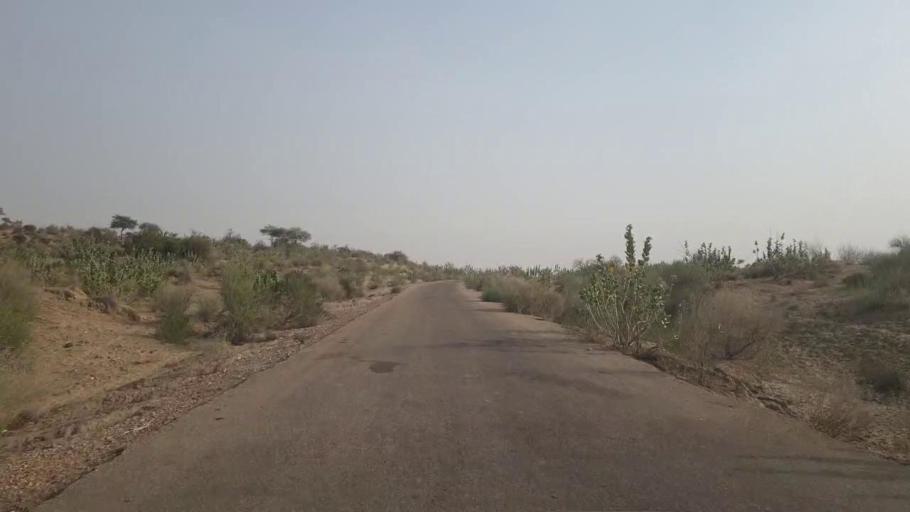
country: PK
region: Sindh
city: Chor
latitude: 25.4845
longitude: 69.9747
